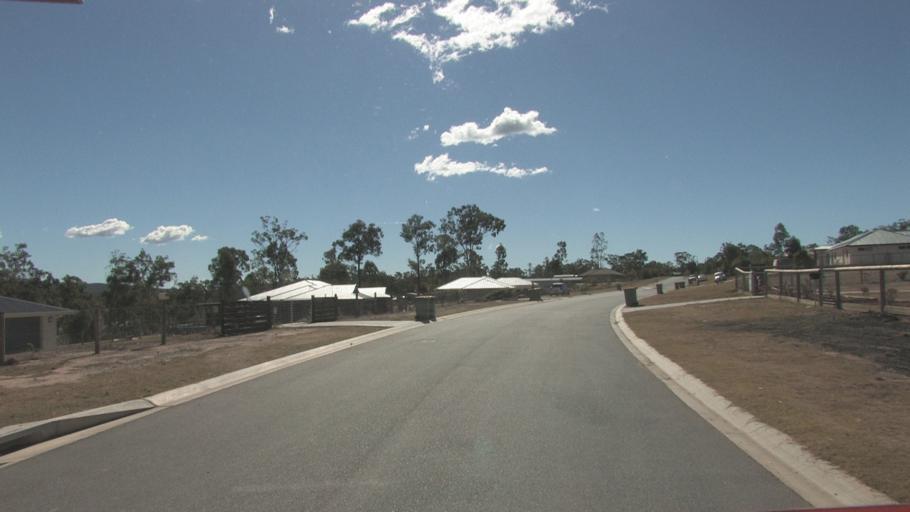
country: AU
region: Queensland
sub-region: Logan
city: North Maclean
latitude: -27.7596
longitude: 152.9339
